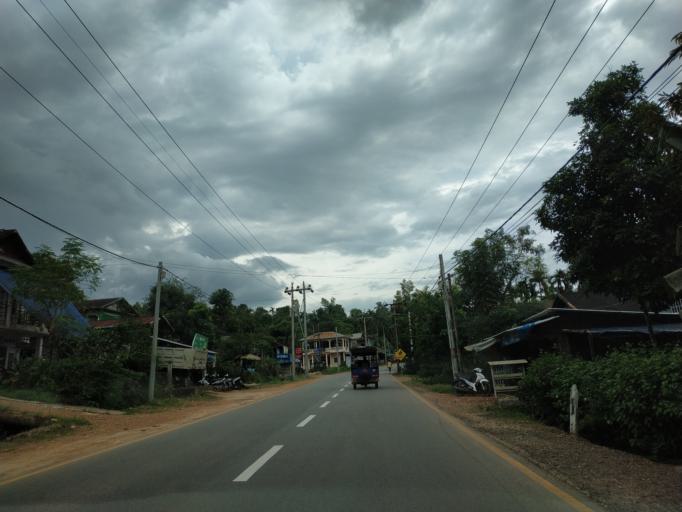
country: MM
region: Tanintharyi
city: Dawei
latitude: 13.9615
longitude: 98.2434
